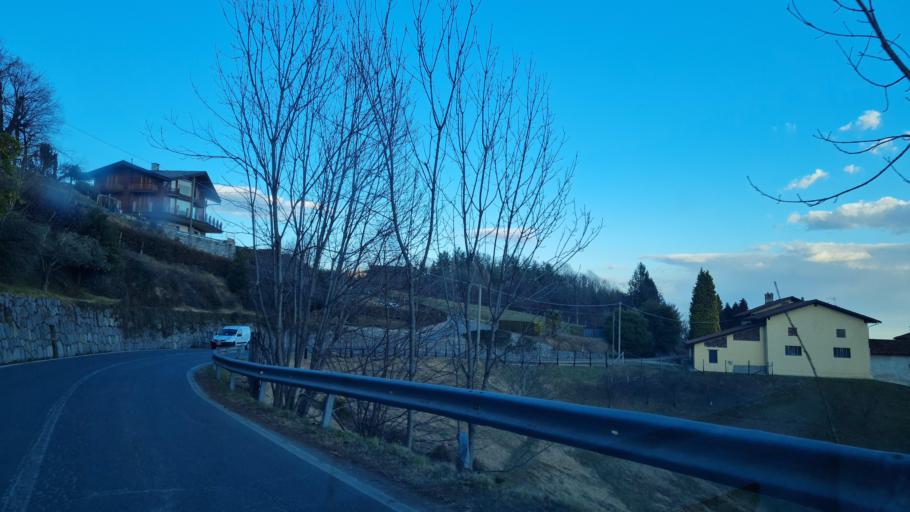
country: IT
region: Piedmont
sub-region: Provincia di Biella
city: Sordevolo
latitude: 45.5790
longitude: 7.9853
